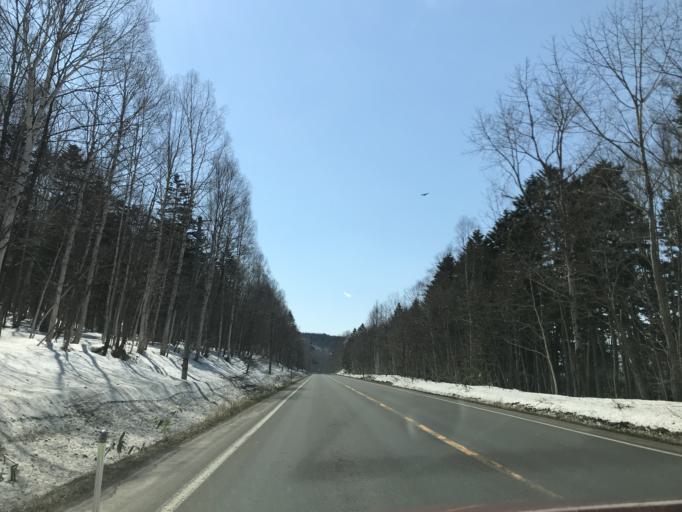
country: JP
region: Hokkaido
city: Nayoro
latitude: 44.7157
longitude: 142.2725
